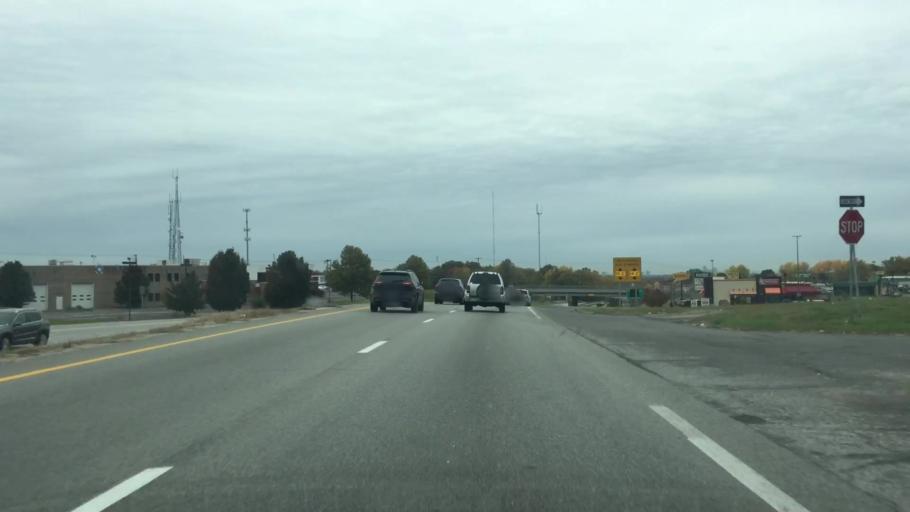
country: US
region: Missouri
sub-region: Jackson County
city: Raytown
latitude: 38.9986
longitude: -94.4796
